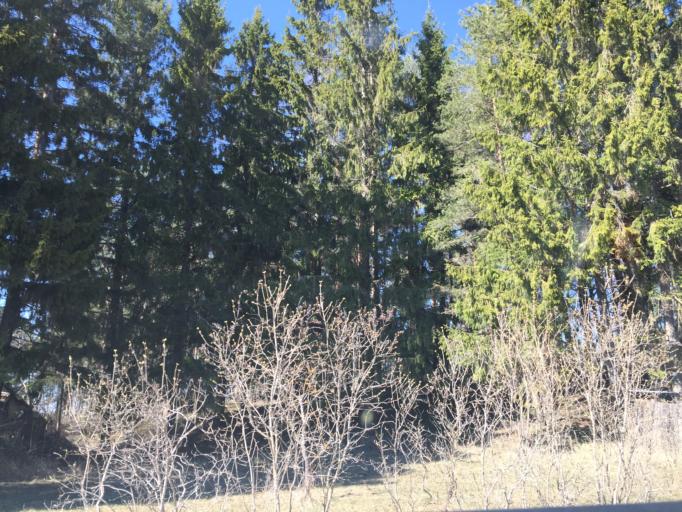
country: EE
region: Jogevamaa
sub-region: Mustvee linn
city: Mustvee
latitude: 58.9824
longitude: 27.1789
